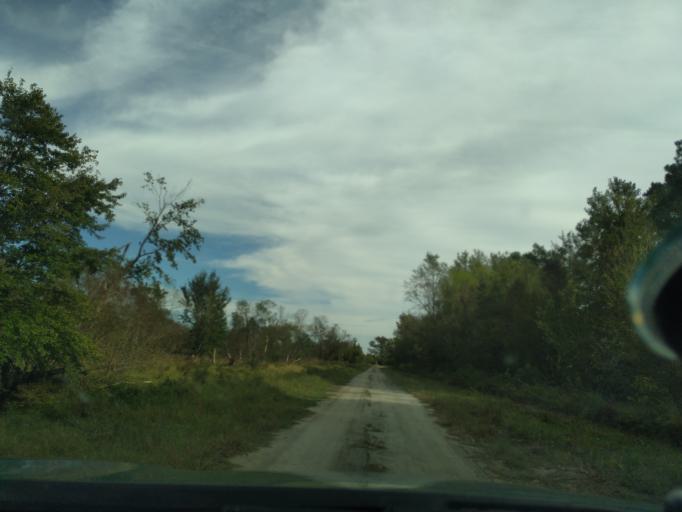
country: US
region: North Carolina
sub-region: Beaufort County
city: Belhaven
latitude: 35.7286
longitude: -76.5734
